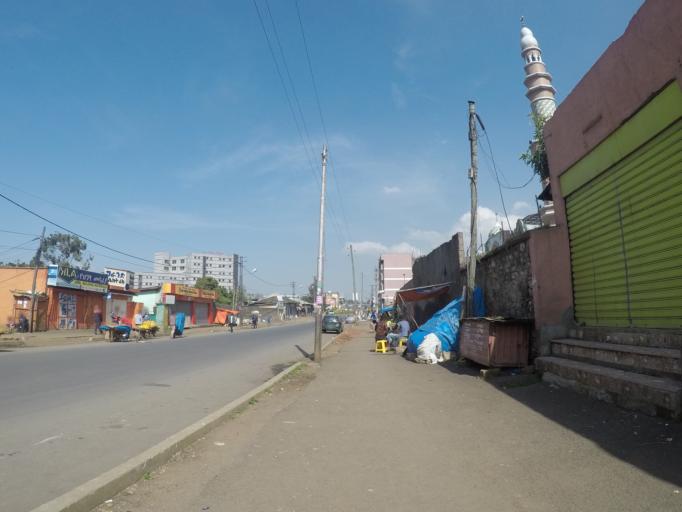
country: ET
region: Adis Abeba
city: Addis Ababa
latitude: 9.0317
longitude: 38.7488
